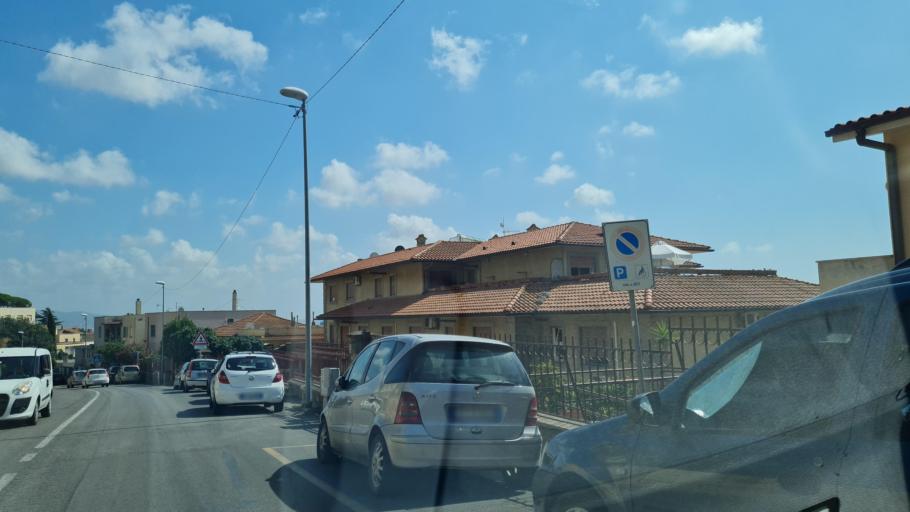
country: IT
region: Latium
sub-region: Provincia di Viterbo
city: Tarquinia
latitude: 42.2514
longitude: 11.7529
